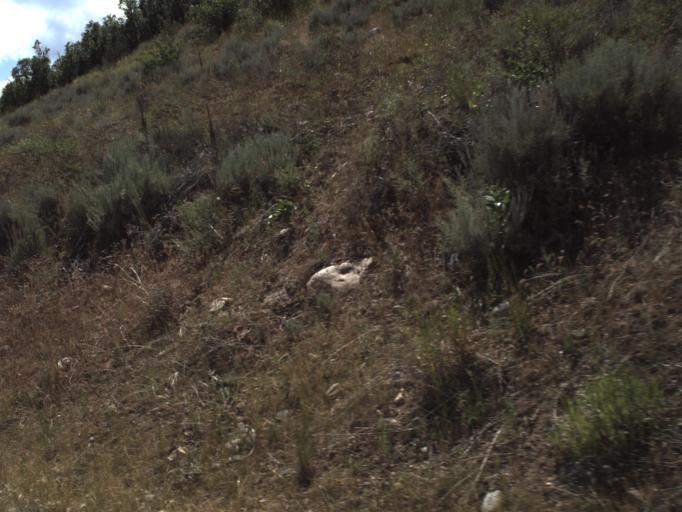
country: US
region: Utah
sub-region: Weber County
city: Wolf Creek
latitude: 41.3373
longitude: -111.6064
